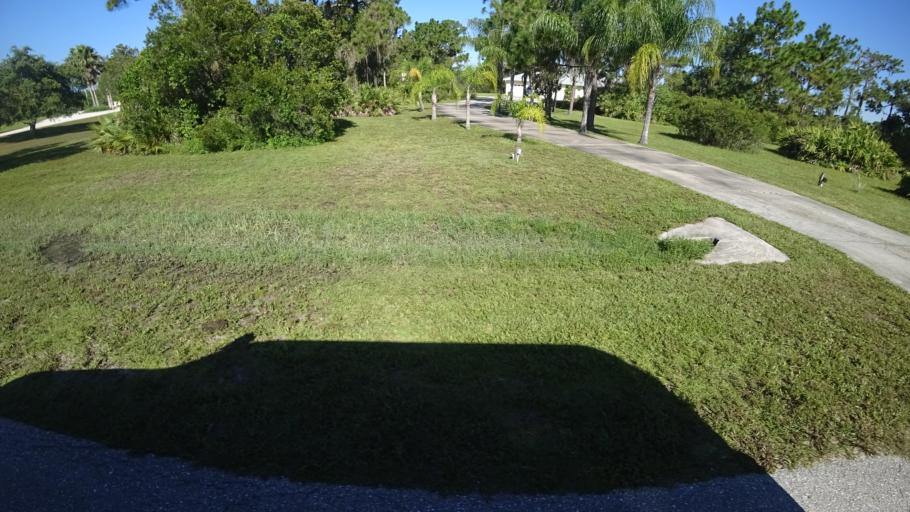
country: US
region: Florida
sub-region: Sarasota County
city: The Meadows
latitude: 27.4104
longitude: -82.3162
